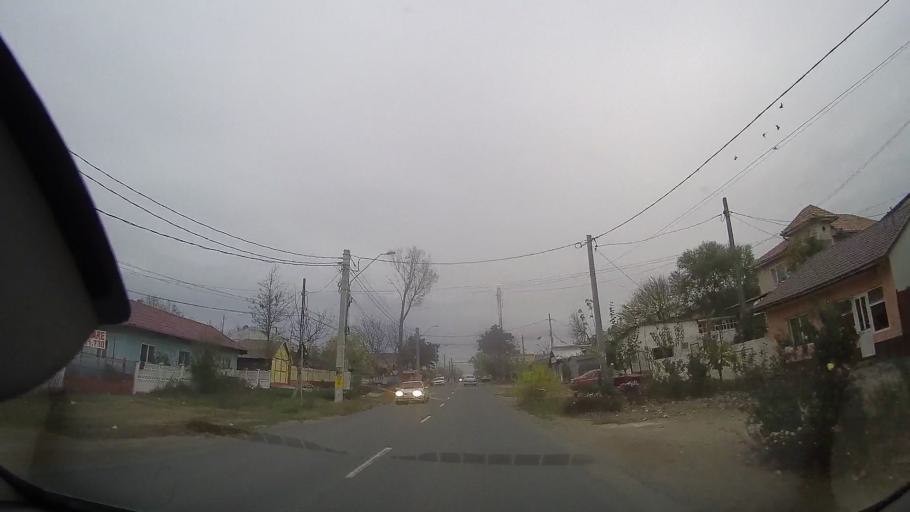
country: RO
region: Ialomita
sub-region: Oras Amara
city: Amara
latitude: 44.6130
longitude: 27.3144
